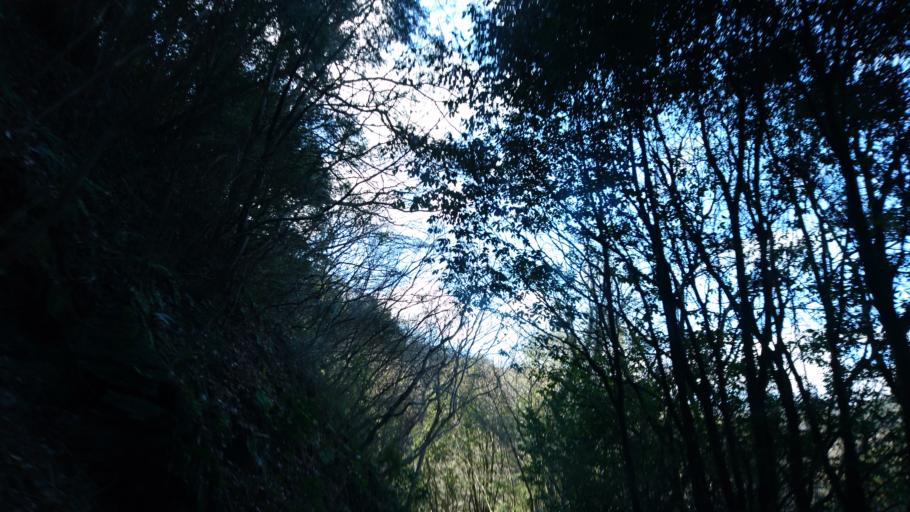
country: JP
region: Okayama
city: Takahashi
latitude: 34.8655
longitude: 133.5704
